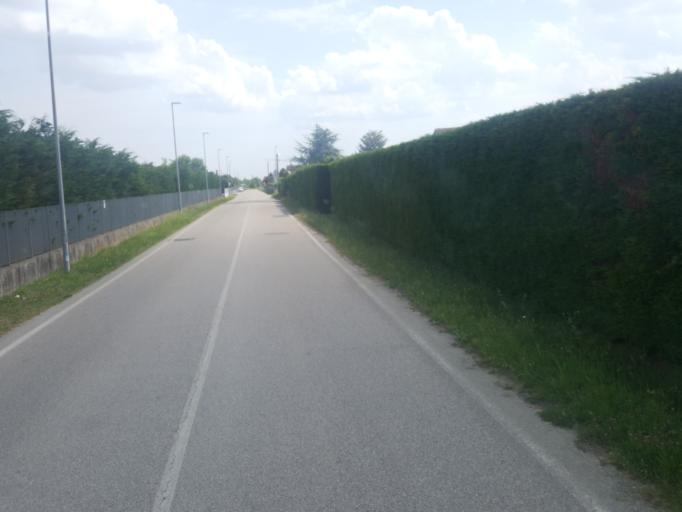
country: IT
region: Veneto
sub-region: Provincia di Padova
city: Vallonga
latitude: 45.2744
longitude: 12.0895
